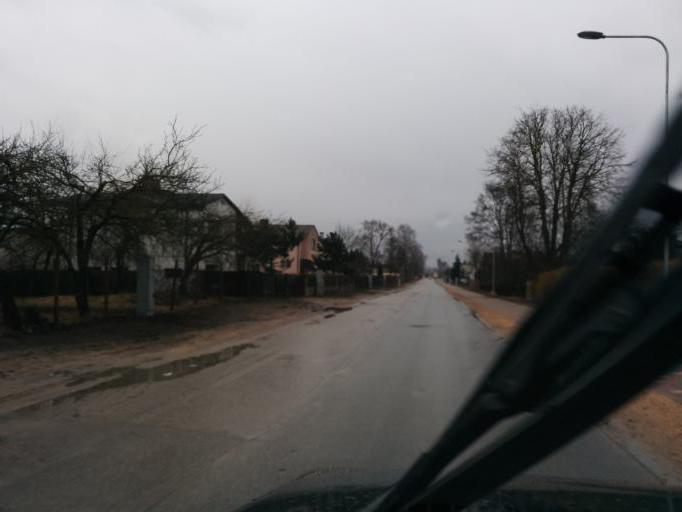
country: LV
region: Kekava
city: Balozi
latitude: 56.8795
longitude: 24.1750
